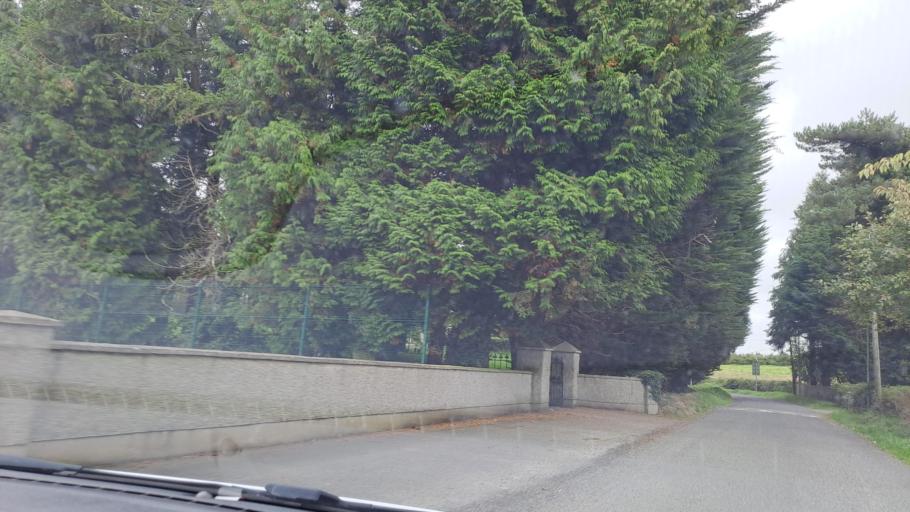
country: IE
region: Ulster
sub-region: County Monaghan
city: Carrickmacross
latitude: 54.0286
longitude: -6.7517
